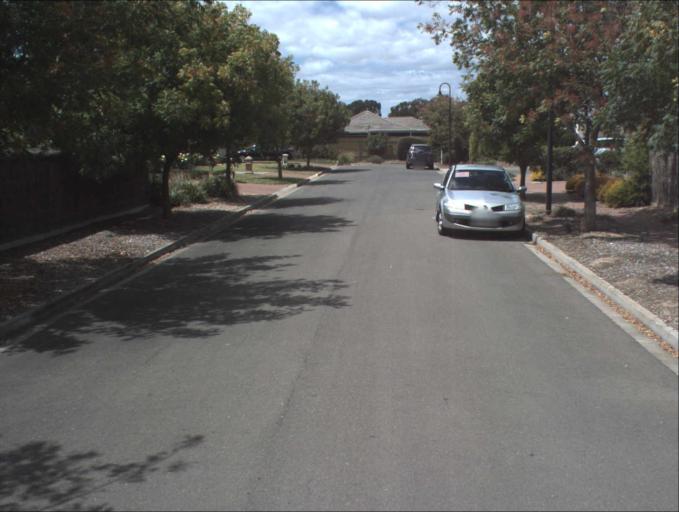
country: AU
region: South Australia
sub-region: Port Adelaide Enfield
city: Enfield
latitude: -34.8592
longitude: 138.6235
